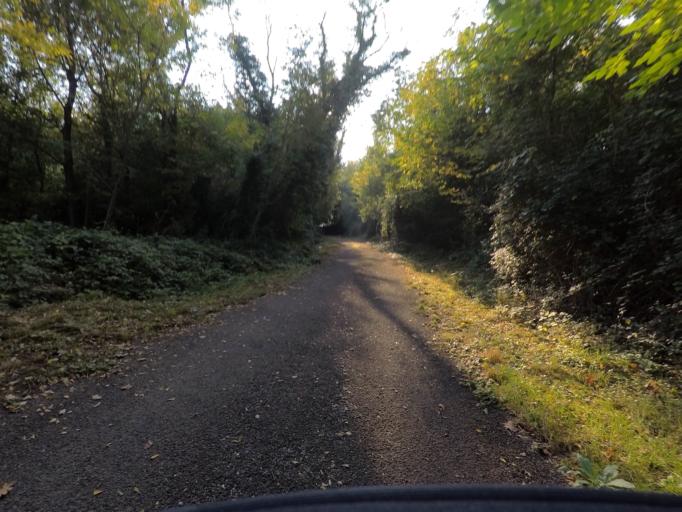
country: IT
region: Friuli Venezia Giulia
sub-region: Provincia di Udine
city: Artegna
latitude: 46.2471
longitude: 13.1450
